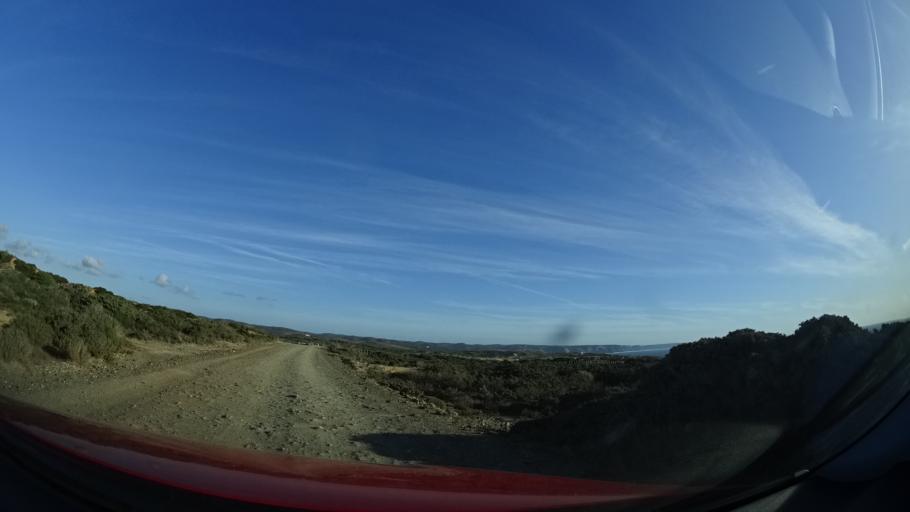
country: PT
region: Faro
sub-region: Vila do Bispo
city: Vila do Bispo
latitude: 37.1919
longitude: -8.9106
